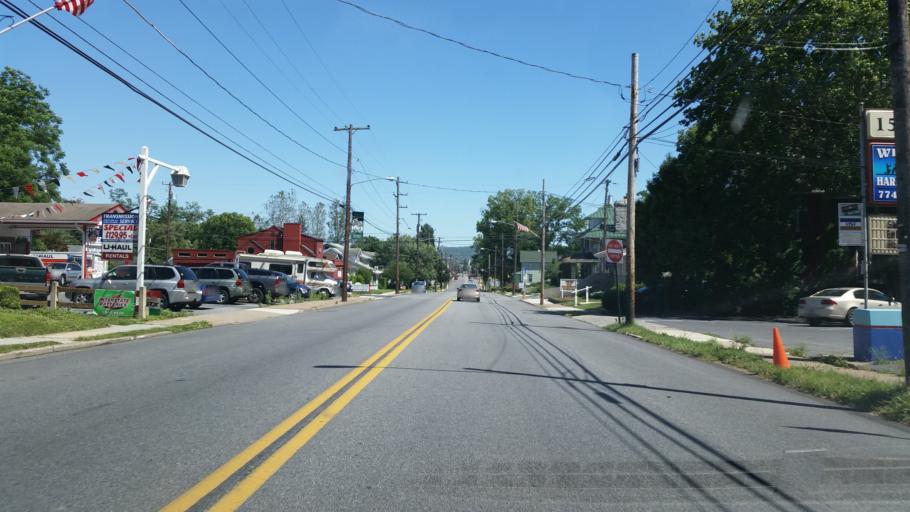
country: US
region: Pennsylvania
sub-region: Cumberland County
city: New Cumberland
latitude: 40.2356
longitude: -76.8776
